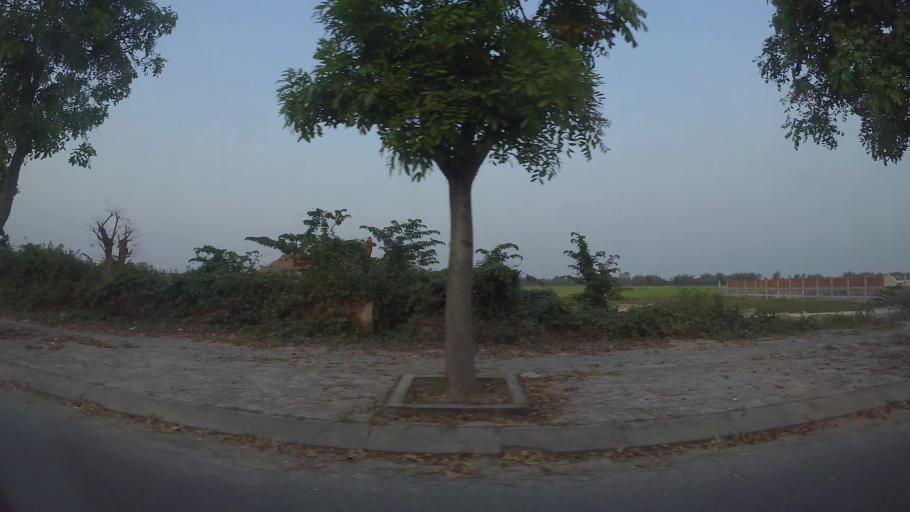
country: VN
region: Da Nang
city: Cam Le
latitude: 15.9639
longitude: 108.2124
